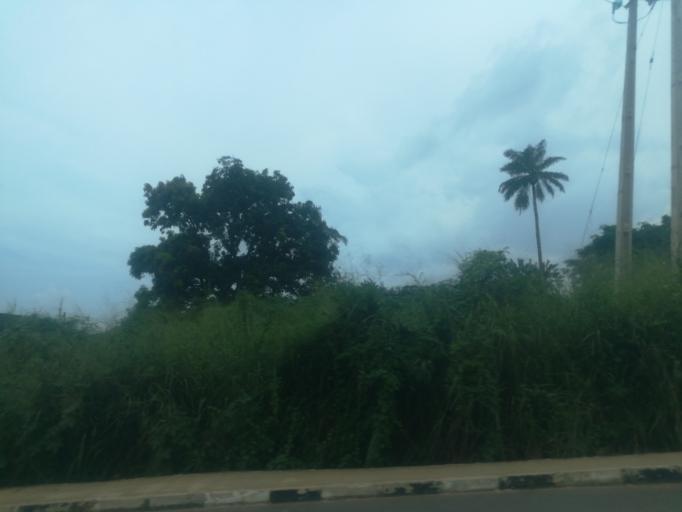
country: NG
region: Oyo
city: Ibadan
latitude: 7.3751
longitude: 3.8285
